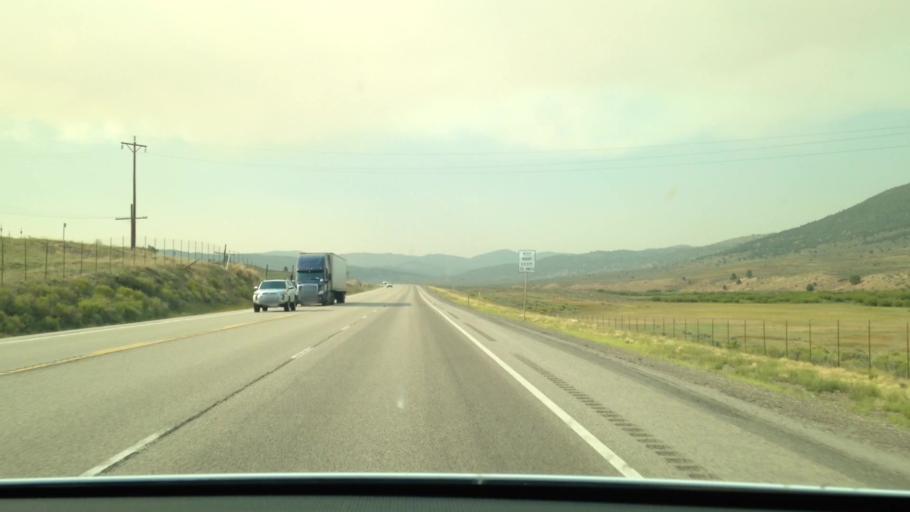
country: US
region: Utah
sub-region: Carbon County
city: Helper
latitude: 39.8883
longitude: -111.0491
